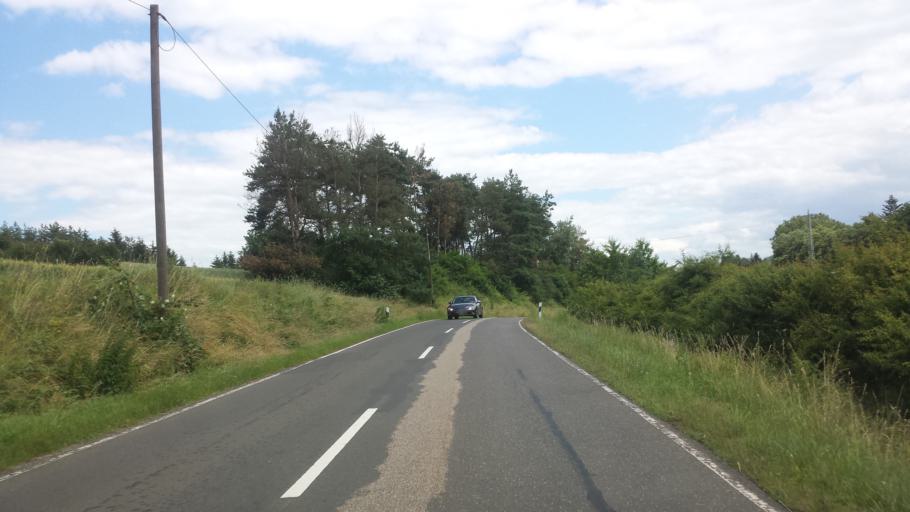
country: DE
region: Rheinland-Pfalz
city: Ramsen
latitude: 49.5347
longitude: 8.0008
